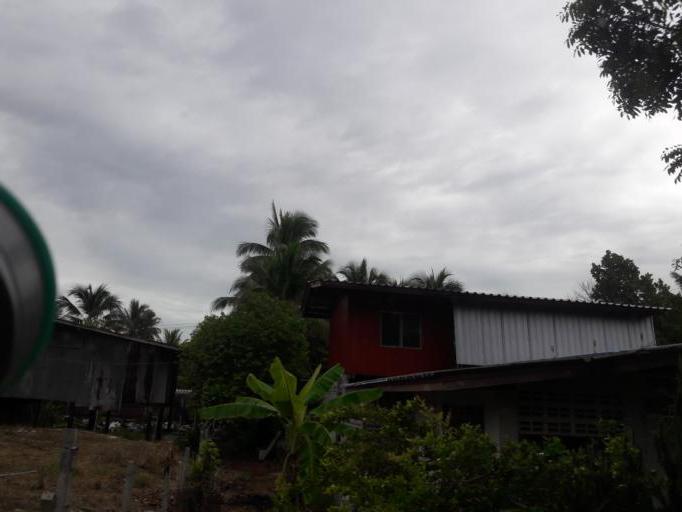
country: TH
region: Ratchaburi
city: Damnoen Saduak
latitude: 13.5269
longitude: 100.0150
